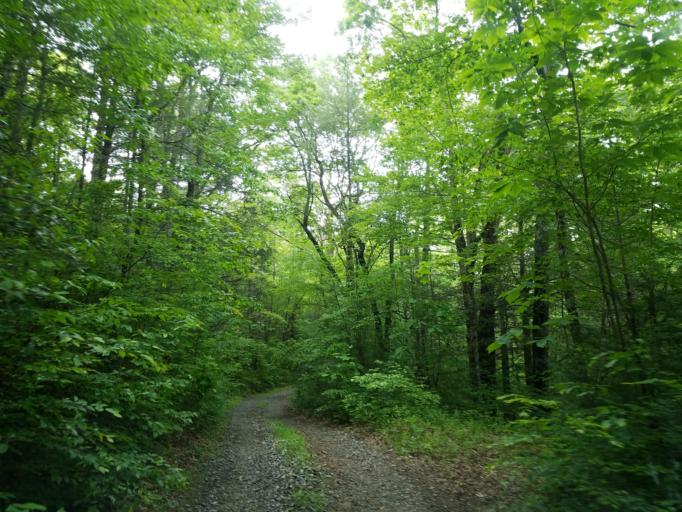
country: US
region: Georgia
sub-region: Union County
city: Blairsville
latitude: 34.7523
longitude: -84.0051
